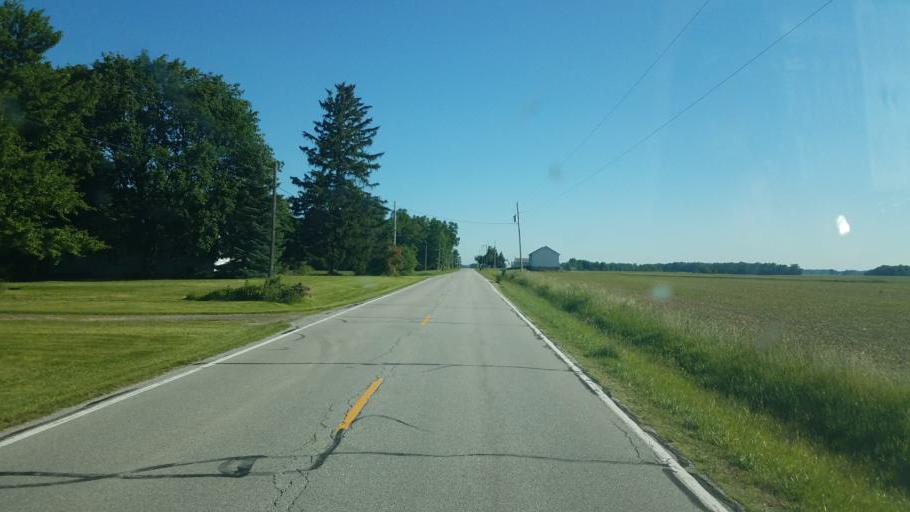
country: US
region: Ohio
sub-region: Crawford County
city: Bucyrus
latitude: 40.7558
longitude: -82.9537
